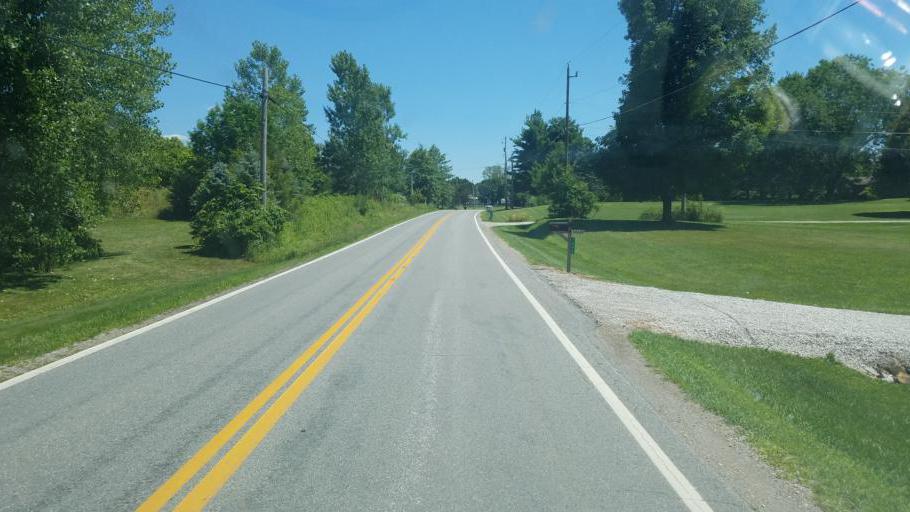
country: US
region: Ohio
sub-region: Delaware County
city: Sunbury
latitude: 40.2341
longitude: -82.8876
